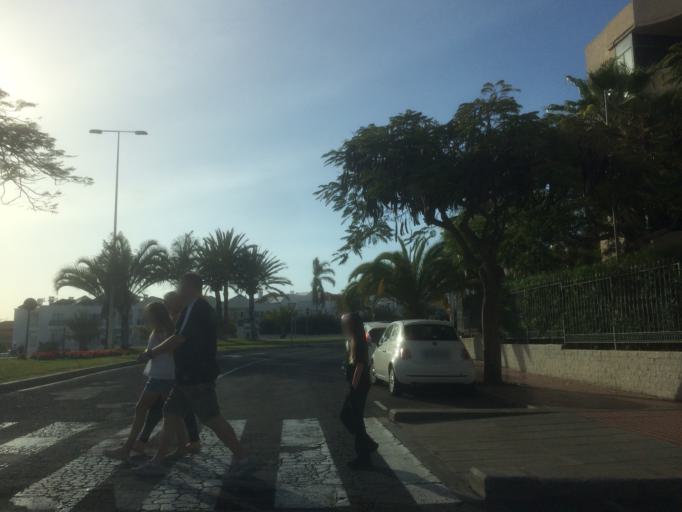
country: ES
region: Canary Islands
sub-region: Provincia de Santa Cruz de Tenerife
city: Playa de las Americas
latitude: 28.0891
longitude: -16.7347
